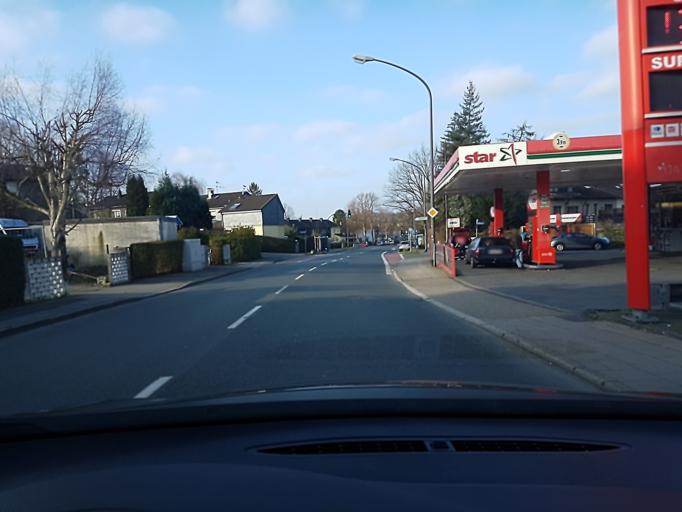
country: DE
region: North Rhine-Westphalia
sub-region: Regierungsbezirk Dusseldorf
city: Essen
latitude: 51.4206
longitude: 7.0919
